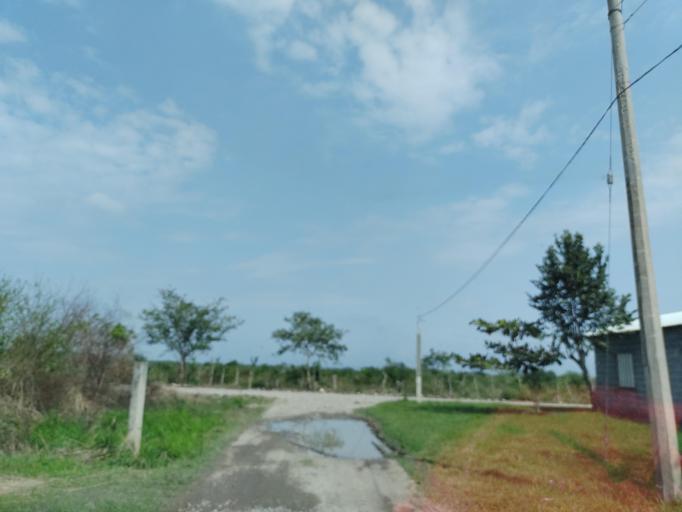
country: MX
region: Puebla
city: Espinal
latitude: 20.2810
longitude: -97.3329
